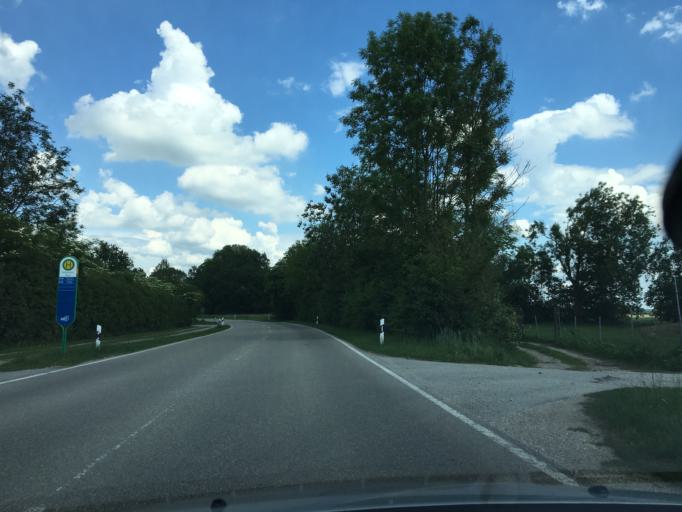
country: DE
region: Bavaria
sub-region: Upper Bavaria
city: Kranzberg
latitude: 48.3742
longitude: 11.6591
